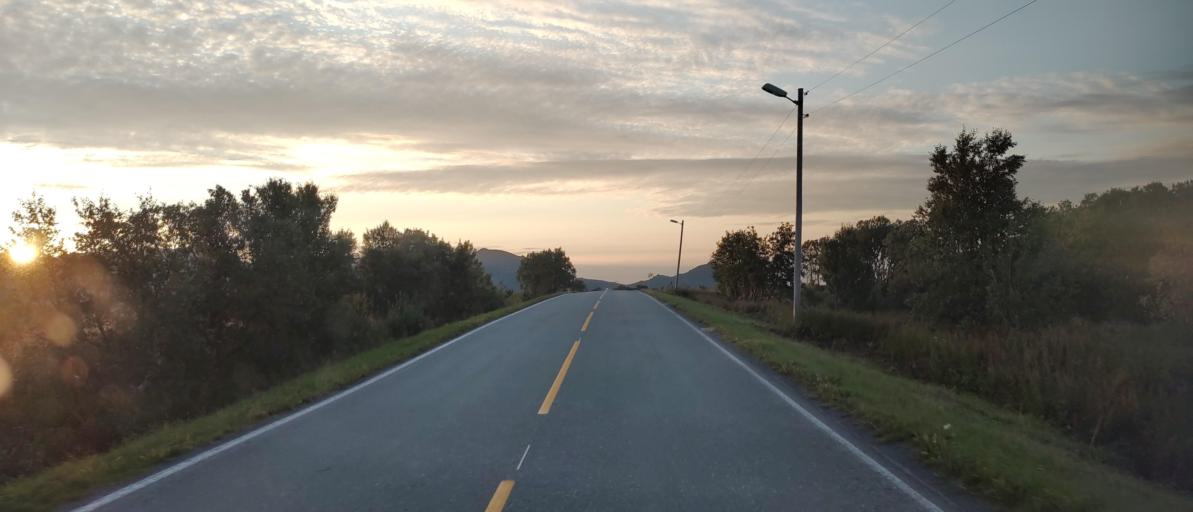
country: NO
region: Nordland
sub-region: Andoy
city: Andenes
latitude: 69.2469
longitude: 16.1147
